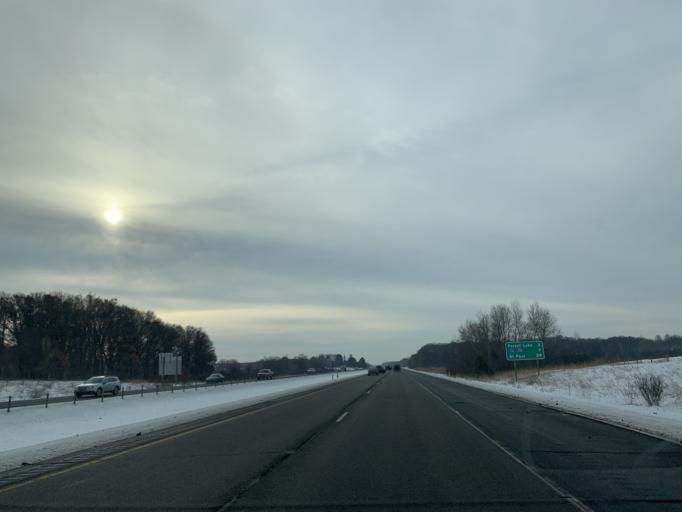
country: US
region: Minnesota
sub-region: Chisago County
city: Wyoming
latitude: 45.3223
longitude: -93.0036
